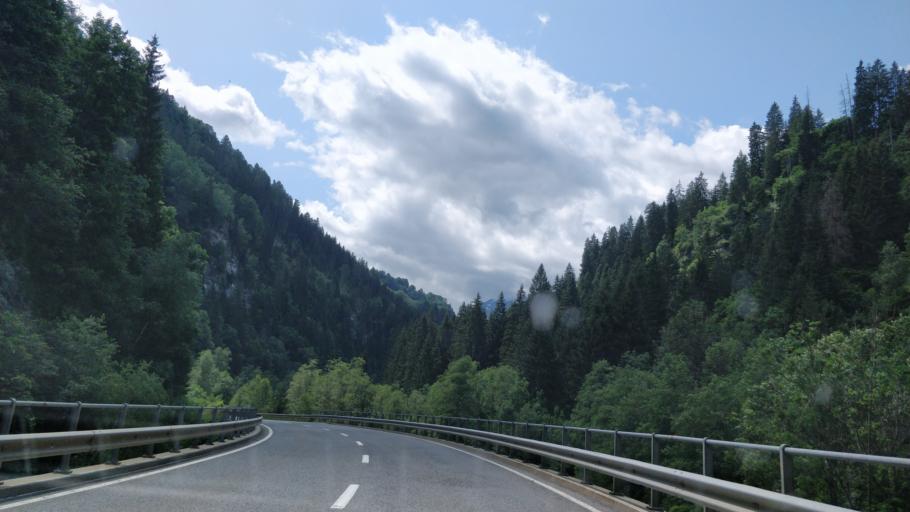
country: CH
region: Grisons
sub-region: Surselva District
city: Ilanz
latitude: 46.7372
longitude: 9.2145
